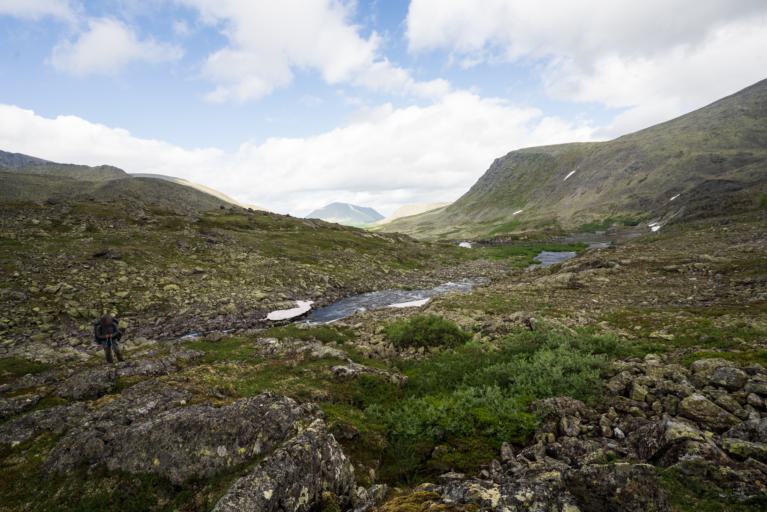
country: RU
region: Komi Republic
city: Synya
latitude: 64.8196
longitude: 59.2503
